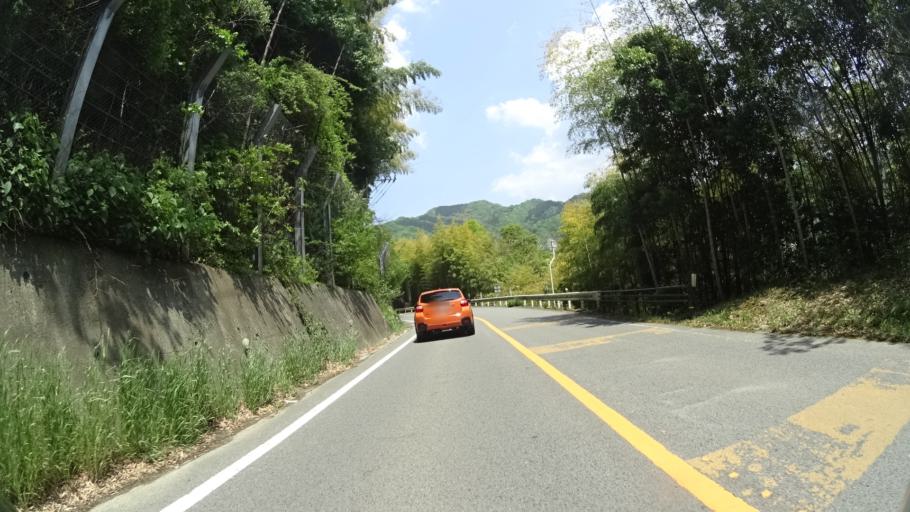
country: JP
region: Ehime
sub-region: Shikoku-chuo Shi
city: Matsuyama
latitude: 33.8833
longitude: 132.8354
